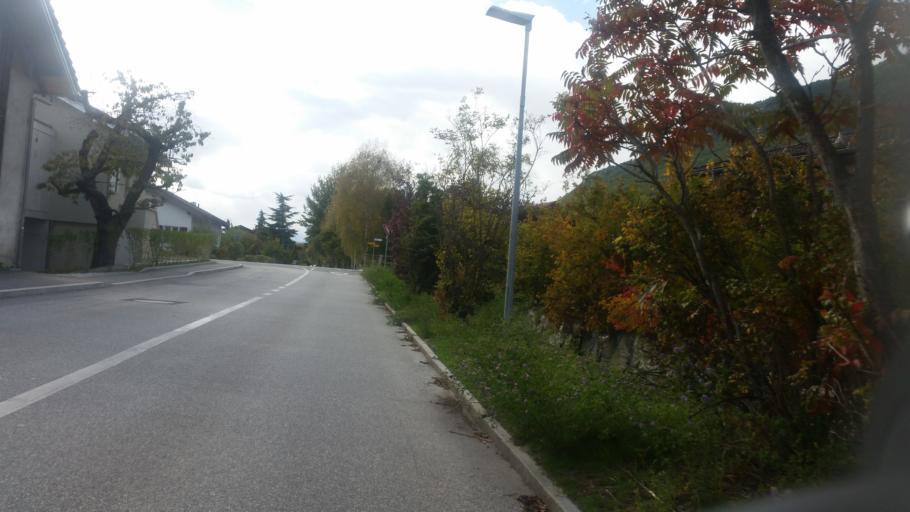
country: CH
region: Valais
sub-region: Sierre District
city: Grone
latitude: 46.2635
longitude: 7.4613
